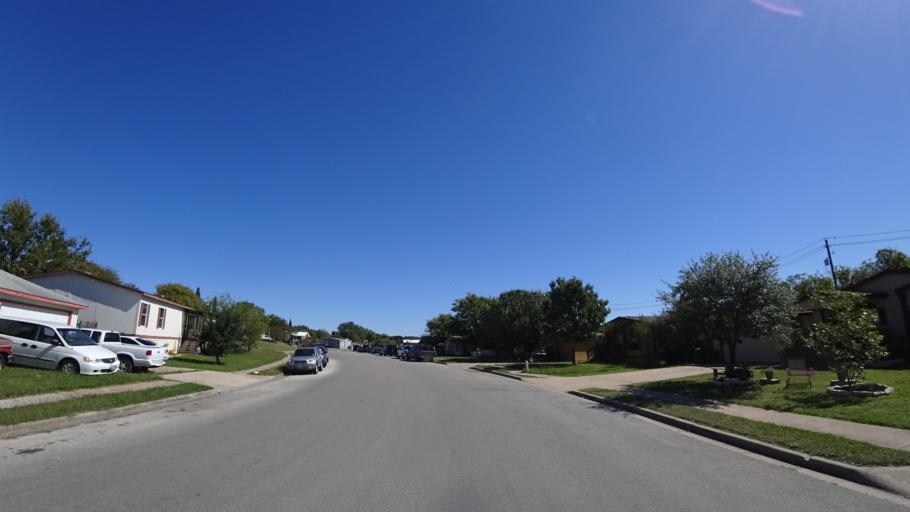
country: US
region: Texas
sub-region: Travis County
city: Hornsby Bend
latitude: 30.3072
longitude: -97.6414
